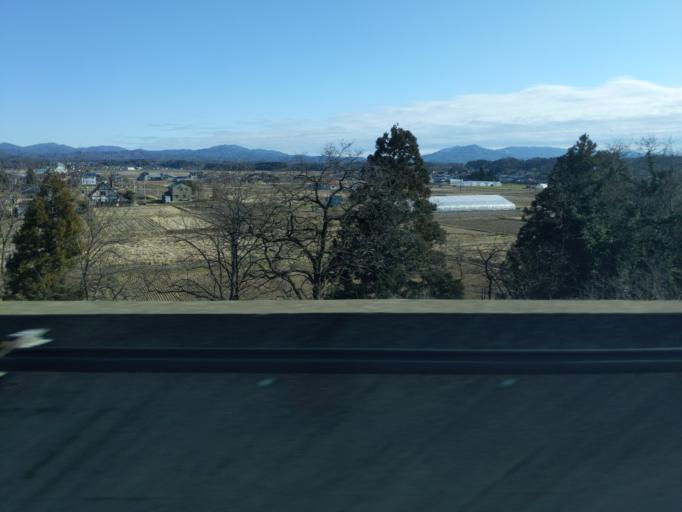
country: JP
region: Fukushima
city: Koriyama
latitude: 37.3505
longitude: 140.3716
